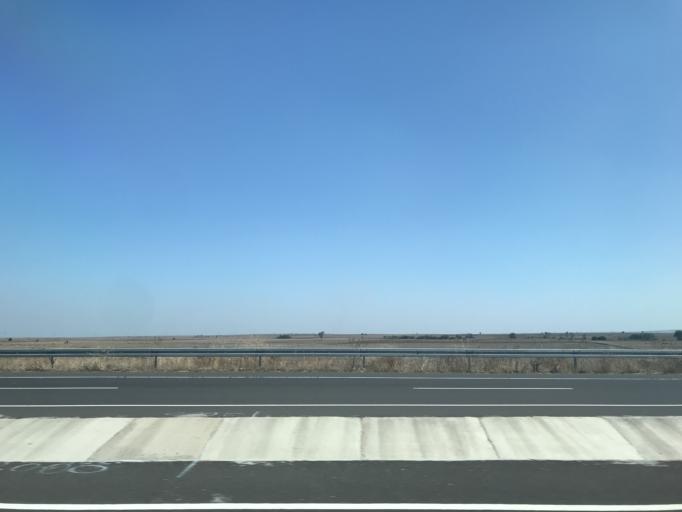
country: TR
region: Tekirdag
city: Muratli
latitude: 41.1868
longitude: 27.5396
